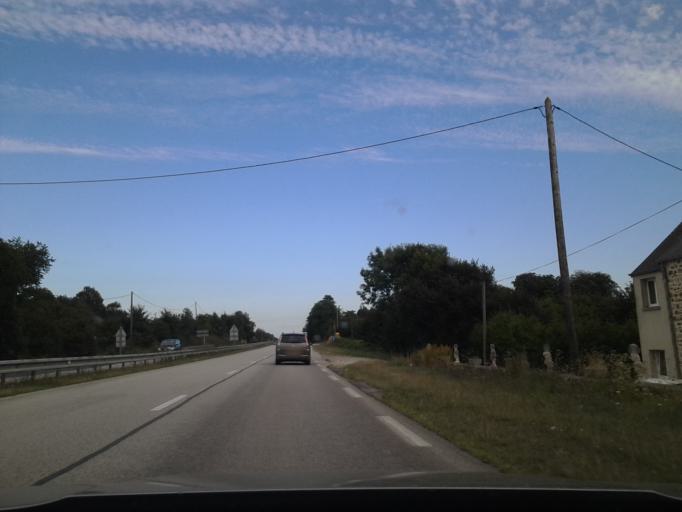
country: FR
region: Lower Normandy
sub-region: Departement de la Manche
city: Valognes
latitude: 49.5278
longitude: -1.5151
